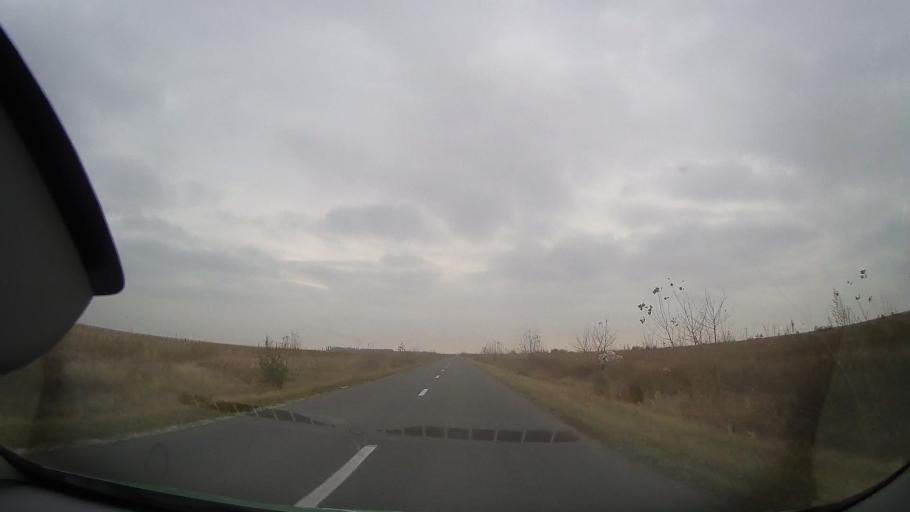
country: RO
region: Ialomita
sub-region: Comuna Garbovi
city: Garbovi
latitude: 44.7513
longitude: 26.7215
